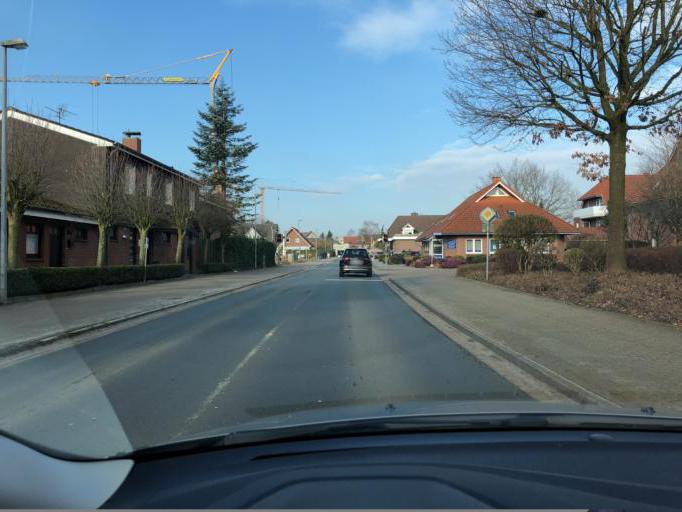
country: DE
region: Lower Saxony
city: Westerstede
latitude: 53.2574
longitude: 7.9344
